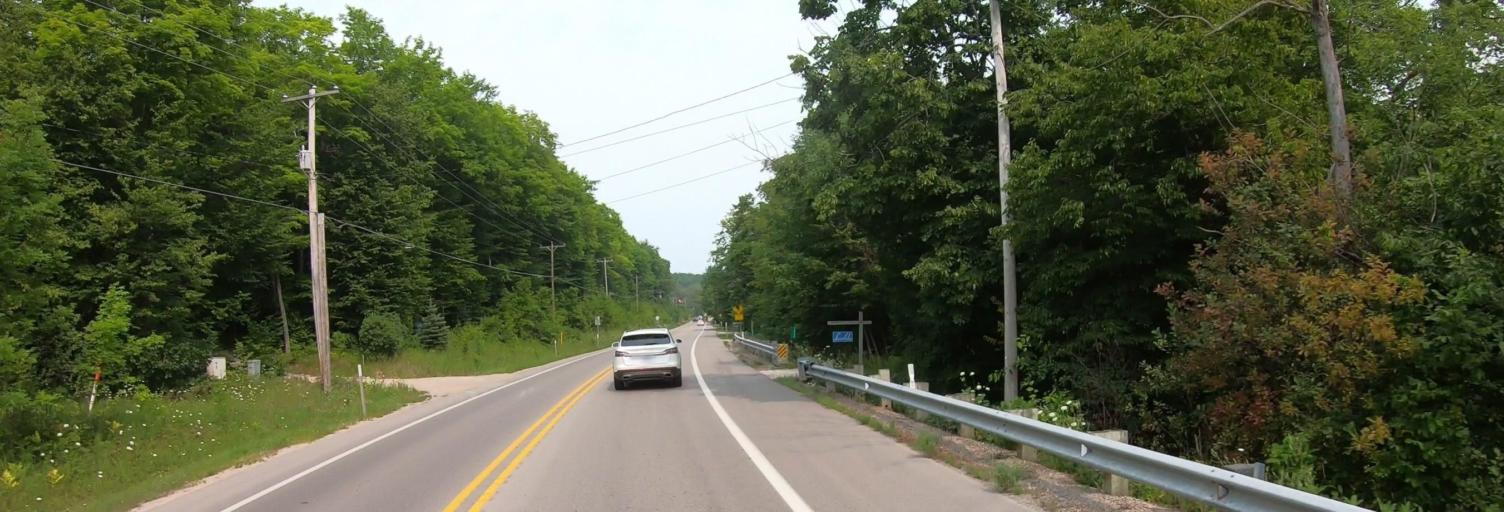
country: US
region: Michigan
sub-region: Leelanau County
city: Leland
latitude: 44.9967
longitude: -85.7713
